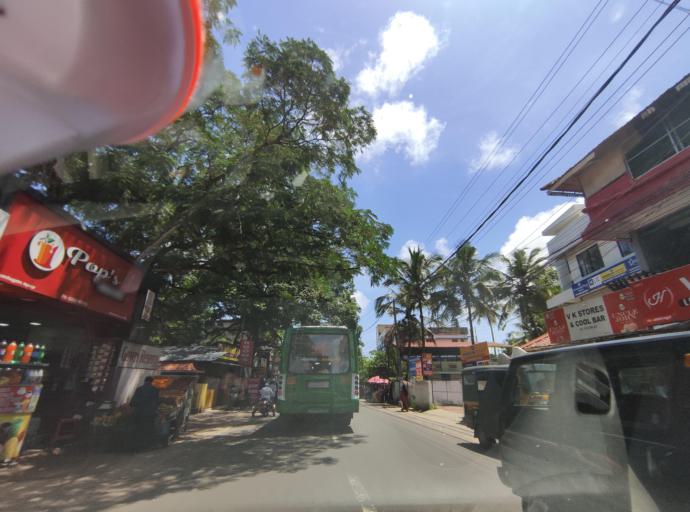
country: IN
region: Kerala
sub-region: Alappuzha
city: Alleppey
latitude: 9.5070
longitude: 76.3400
